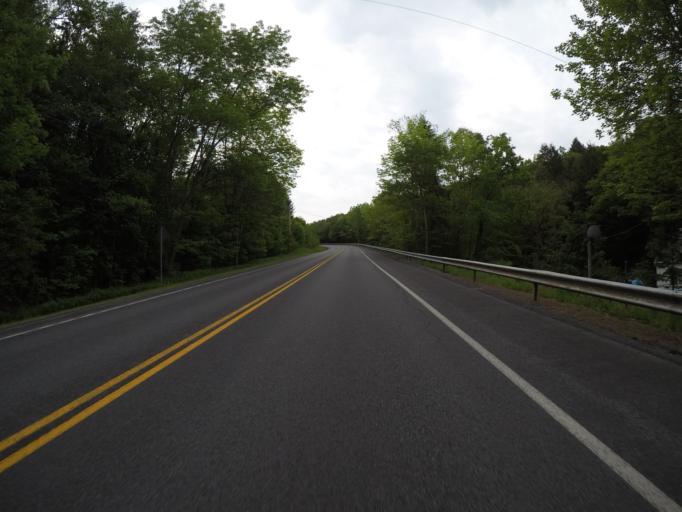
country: US
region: New York
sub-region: Sullivan County
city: Livingston Manor
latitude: 42.0626
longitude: -74.9356
